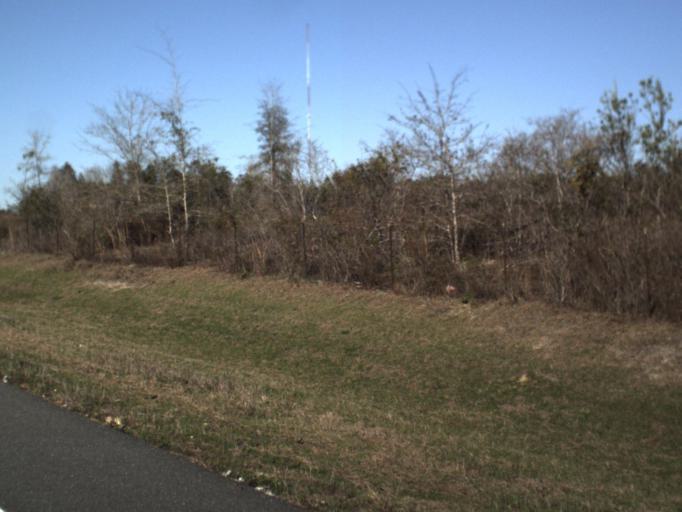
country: US
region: Florida
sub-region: Calhoun County
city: Blountstown
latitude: 30.3610
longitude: -85.2127
